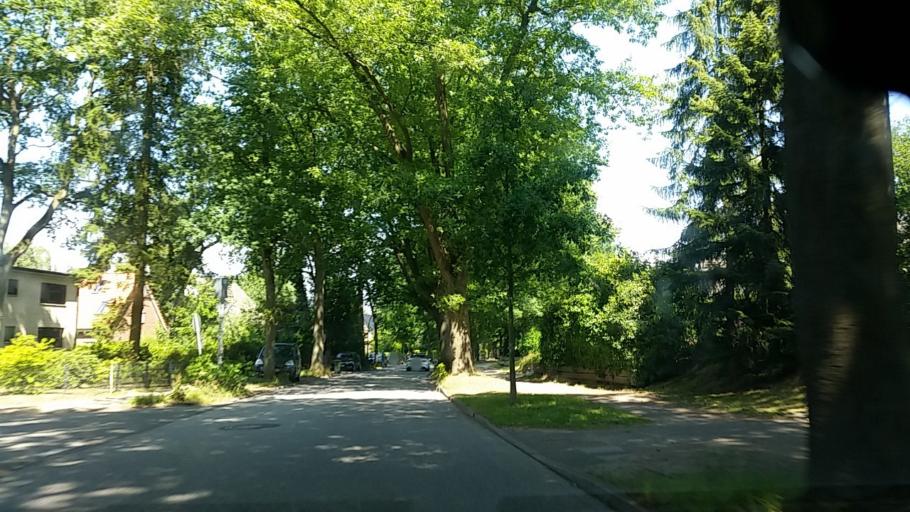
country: DE
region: Schleswig-Holstein
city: Wedel
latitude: 53.5733
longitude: 9.7575
